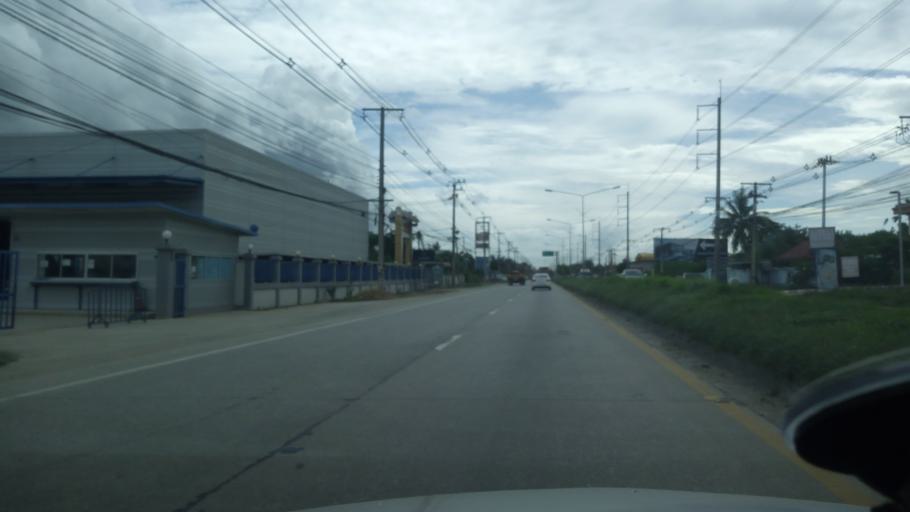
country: TH
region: Chon Buri
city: Phan Thong
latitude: 13.4294
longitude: 101.1237
